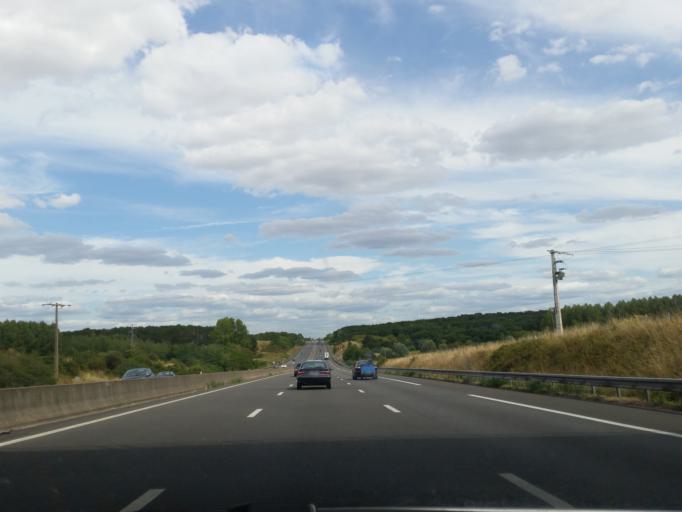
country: FR
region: Centre
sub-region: Departement du Loir-et-Cher
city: Saint-Sulpice-de-Pommeray
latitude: 47.6192
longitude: 1.2484
